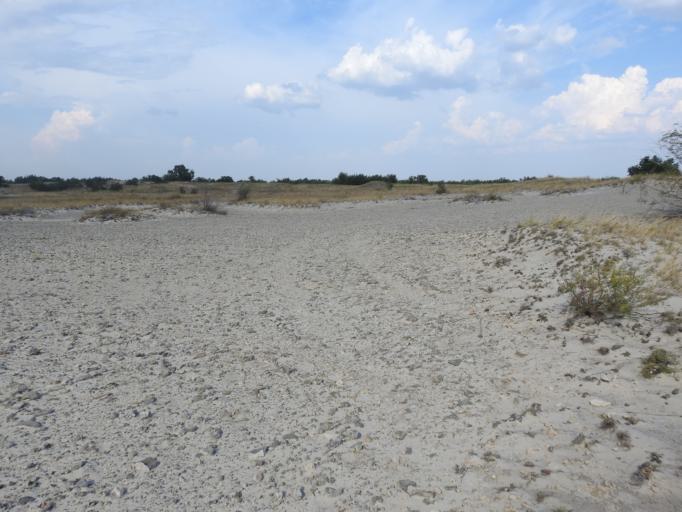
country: RU
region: Saratov
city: Rovnoye
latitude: 50.4805
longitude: 45.7855
